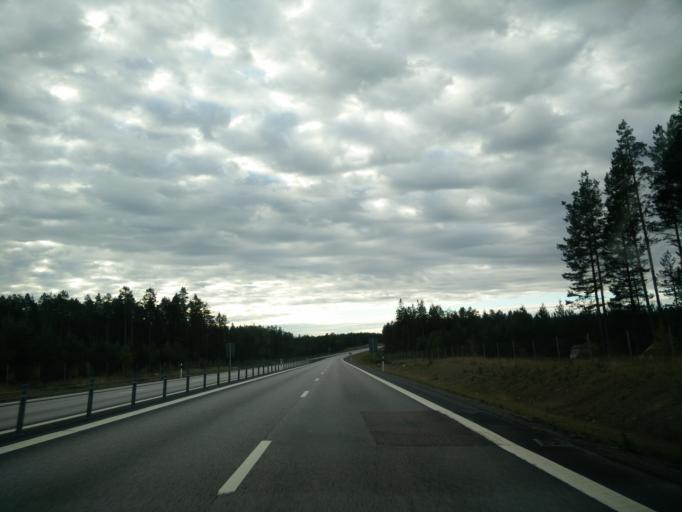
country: SE
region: Gaevleborg
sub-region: Hudiksvalls Kommun
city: Hudiksvall
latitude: 61.7025
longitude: 17.0536
